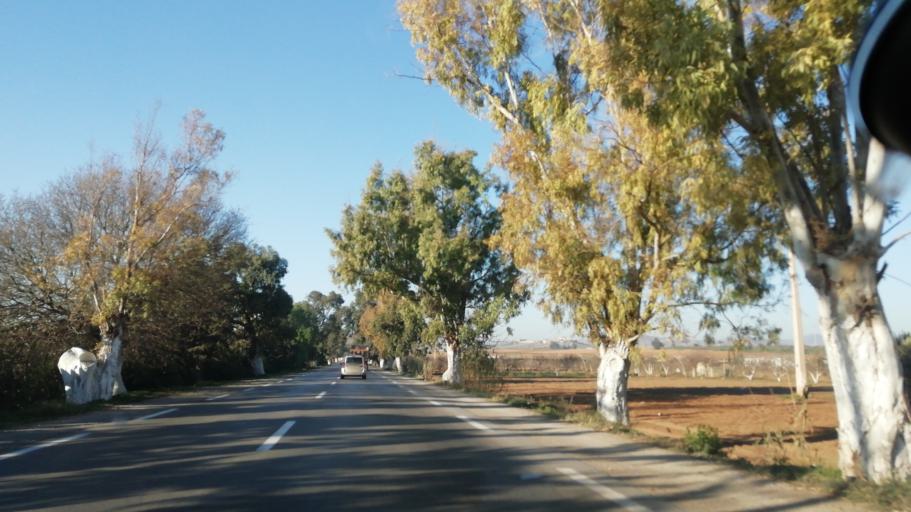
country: DZ
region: Tlemcen
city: Remchi
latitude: 35.0681
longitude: -1.4711
